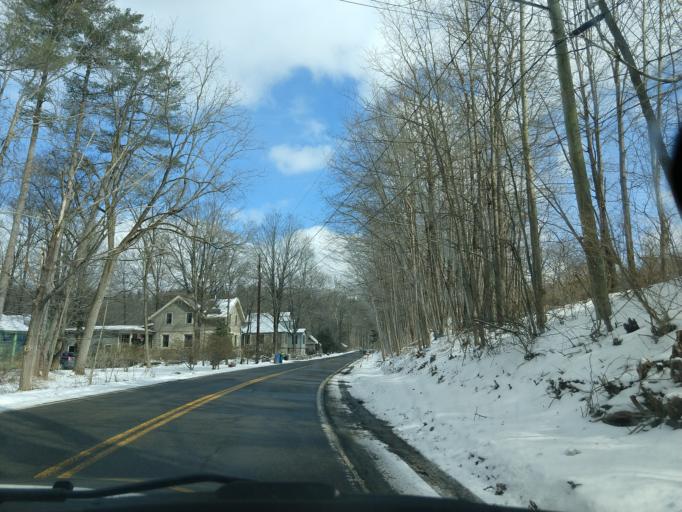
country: US
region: New York
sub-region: Tompkins County
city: Northeast Ithaca
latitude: 42.4524
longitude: -76.4639
